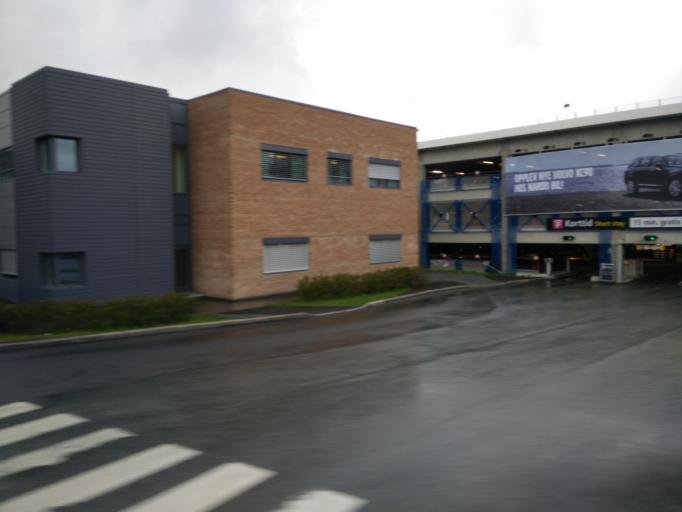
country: NO
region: Nord-Trondelag
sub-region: Stjordal
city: Stjordal
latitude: 63.4528
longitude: 10.9184
